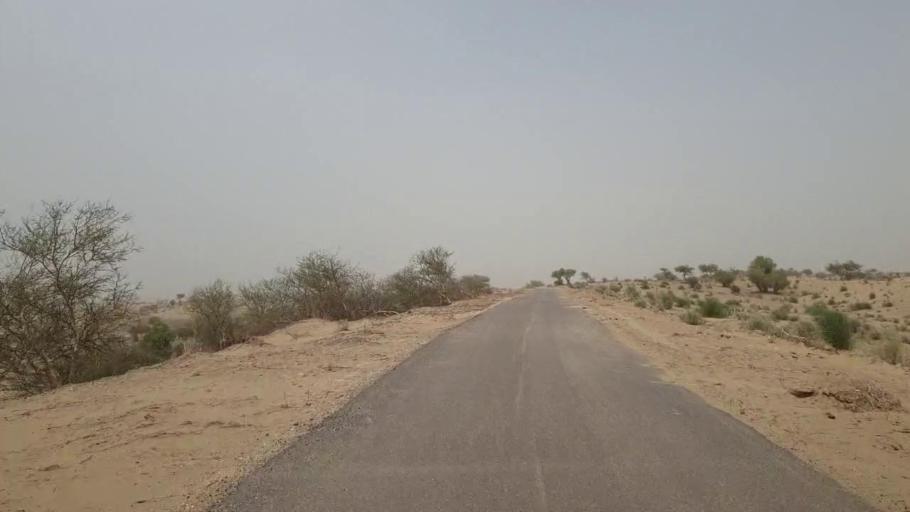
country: PK
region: Sindh
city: Islamkot
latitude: 24.8003
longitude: 70.5200
